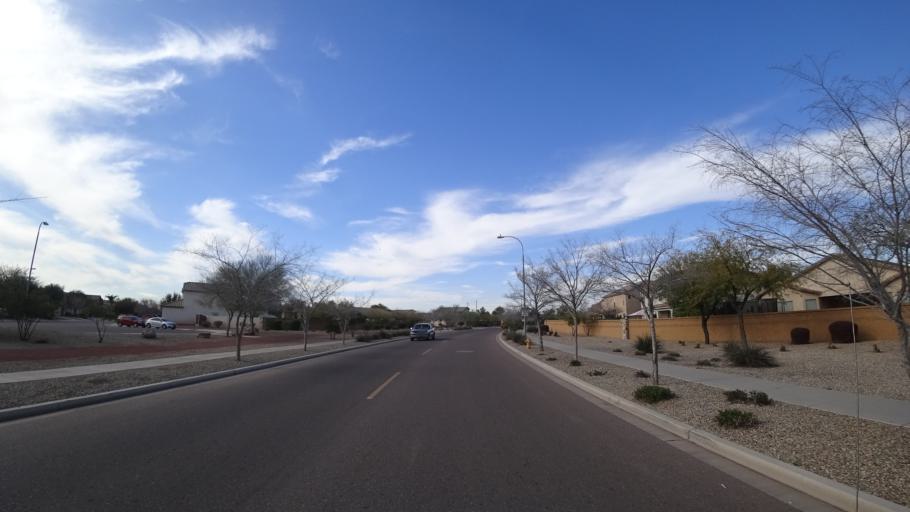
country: US
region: Arizona
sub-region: Maricopa County
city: Tolleson
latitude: 33.4105
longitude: -112.2793
